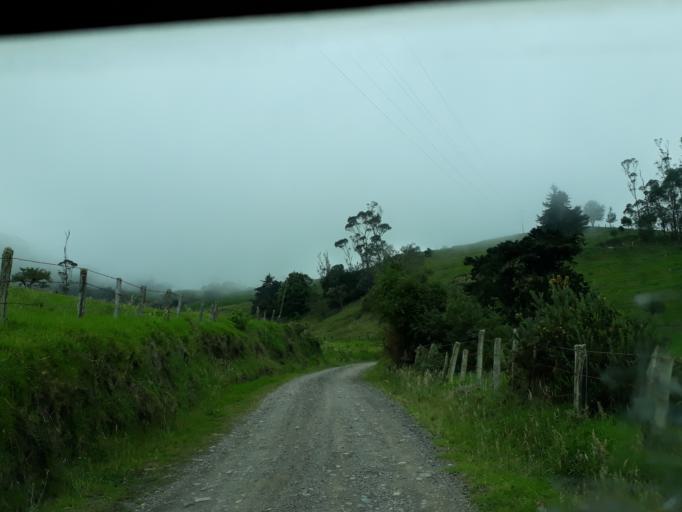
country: CO
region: Cundinamarca
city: Carmen de Carupa
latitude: 5.3735
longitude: -73.9737
